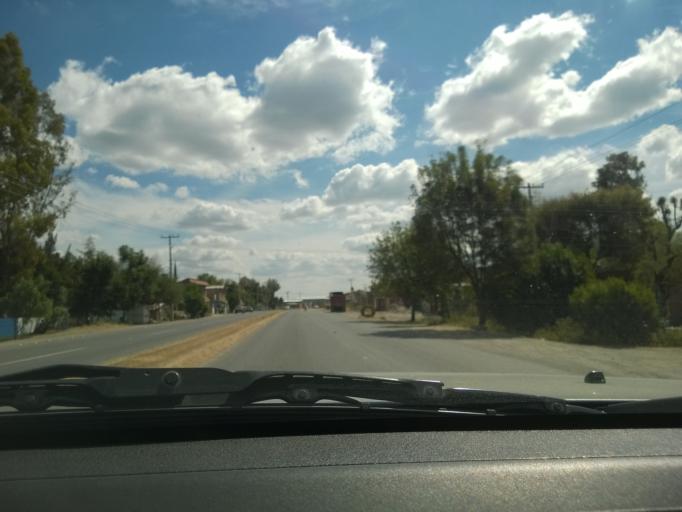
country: MX
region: Guanajuato
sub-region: Leon
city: El CERESO
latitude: 20.9768
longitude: -101.7013
